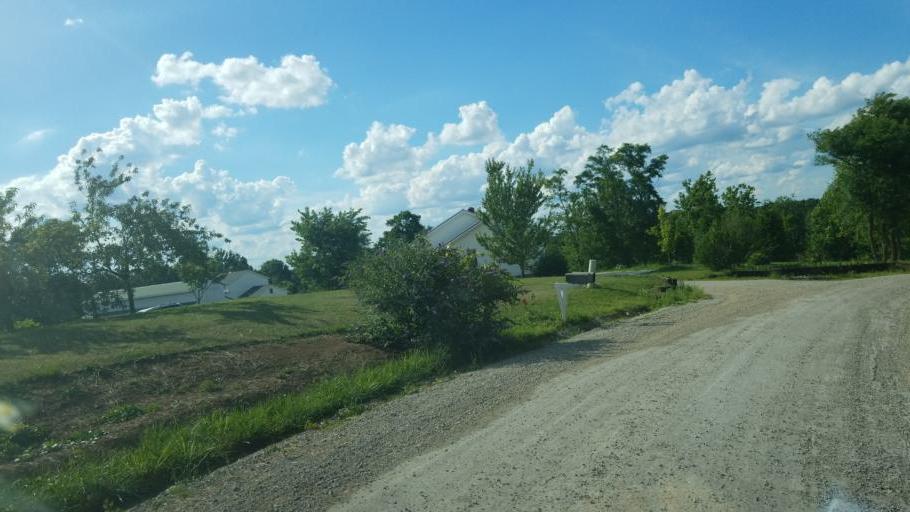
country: US
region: Ohio
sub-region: Gallia County
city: Gallipolis
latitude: 38.7308
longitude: -82.3456
